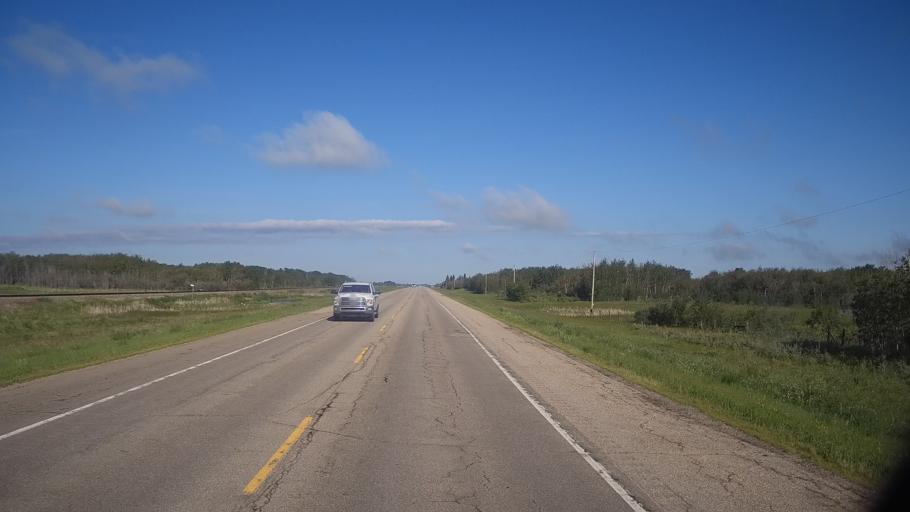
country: CA
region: Saskatchewan
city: Lanigan
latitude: 51.8552
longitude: -105.0867
